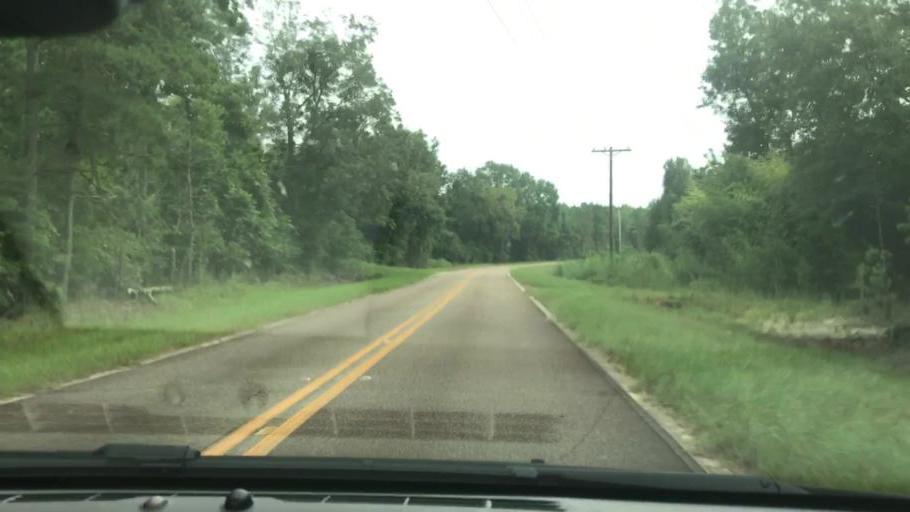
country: US
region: Georgia
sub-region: Stewart County
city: Lumpkin
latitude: 32.0467
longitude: -84.9059
